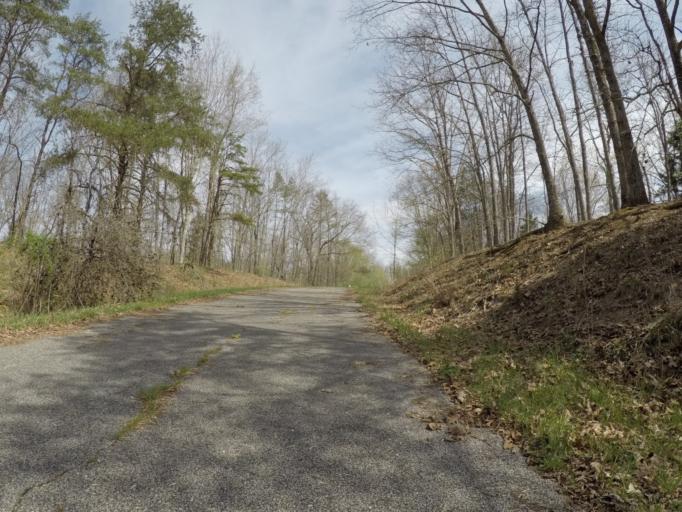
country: US
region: West Virginia
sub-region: Wayne County
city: Lavalette
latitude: 38.3139
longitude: -82.3512
